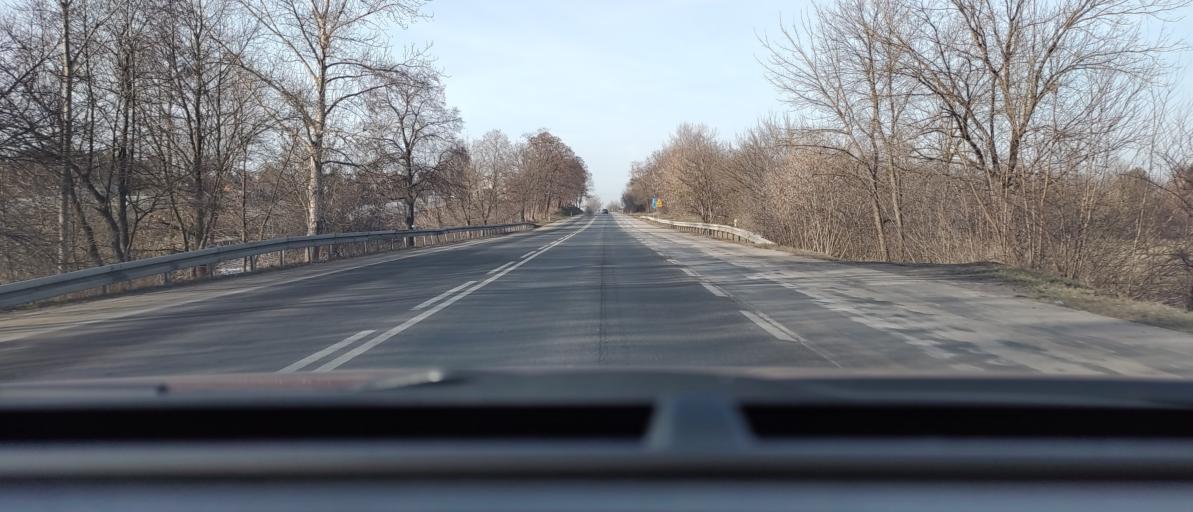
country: PL
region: Masovian Voivodeship
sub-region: Powiat bialobrzeski
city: Promna
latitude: 51.6698
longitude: 20.9455
